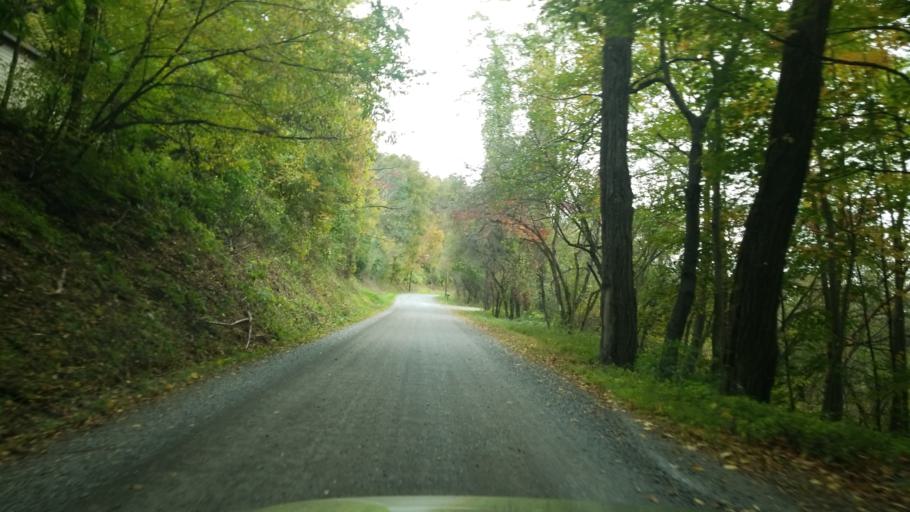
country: US
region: Pennsylvania
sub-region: Clearfield County
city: Curwensville
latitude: 40.9652
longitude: -78.4940
